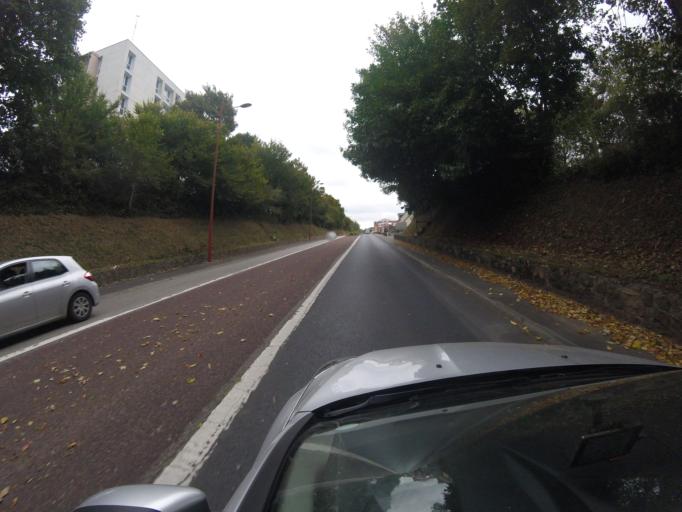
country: FR
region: Lower Normandy
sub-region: Departement de la Manche
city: Cherbourg-Octeville
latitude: 49.6182
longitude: -1.6102
